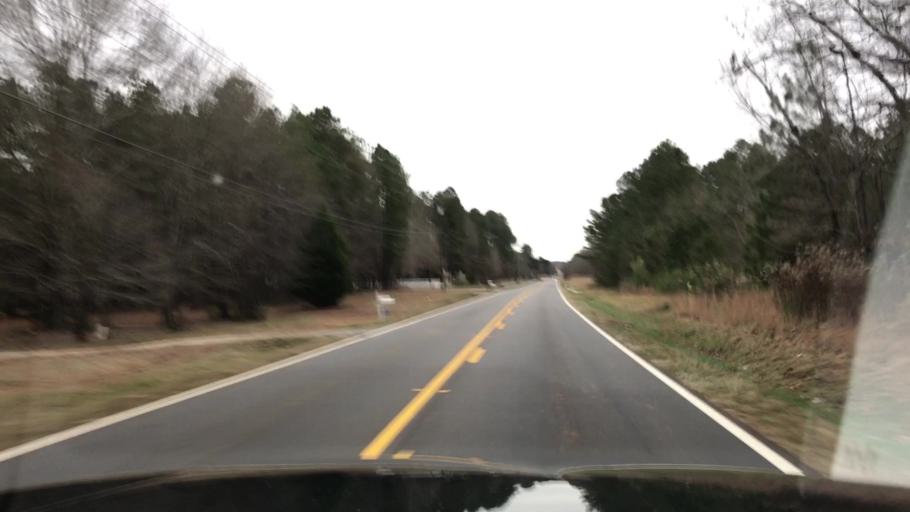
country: US
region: Georgia
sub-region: Barrow County
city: Winder
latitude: 33.8951
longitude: -83.7849
